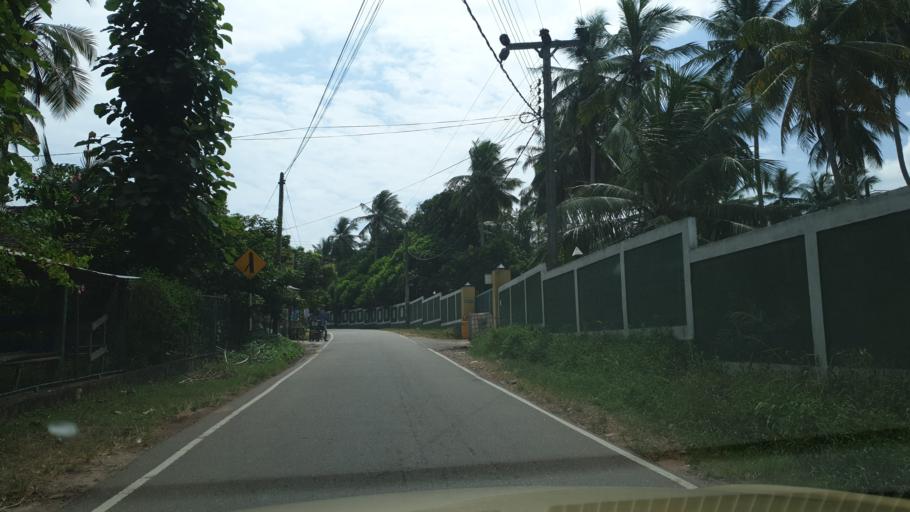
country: LK
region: North Western
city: Kuliyapitiya
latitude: 7.3545
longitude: 79.9766
